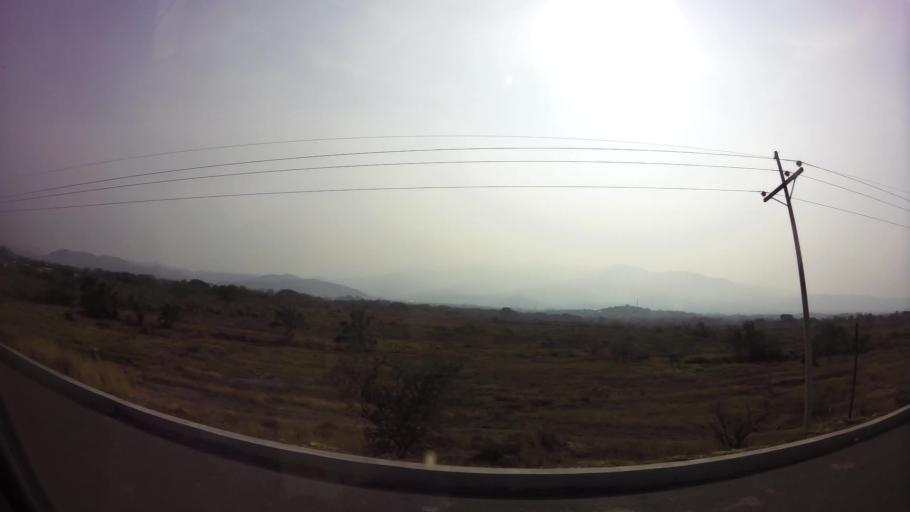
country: HN
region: Comayagua
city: Comayagua
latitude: 14.4388
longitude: -87.6582
